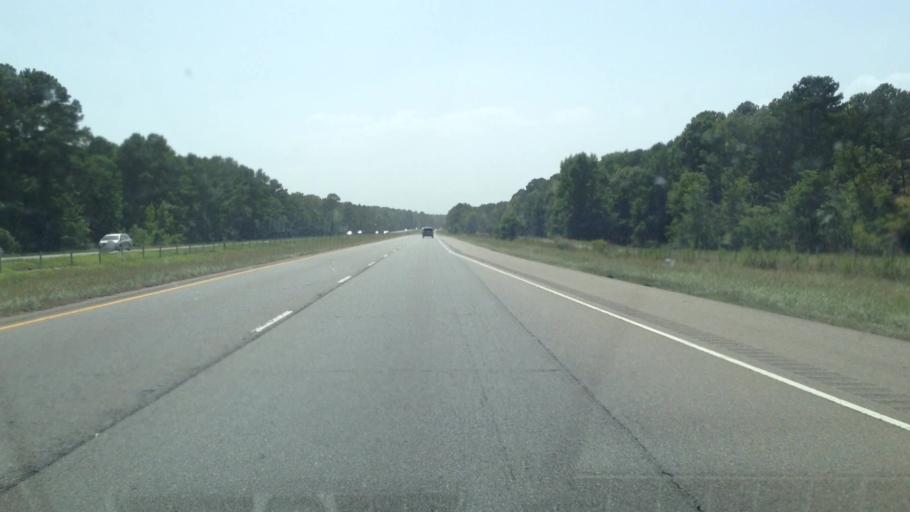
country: US
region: Louisiana
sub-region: Bossier Parish
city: Haughton
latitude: 32.5784
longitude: -93.4392
